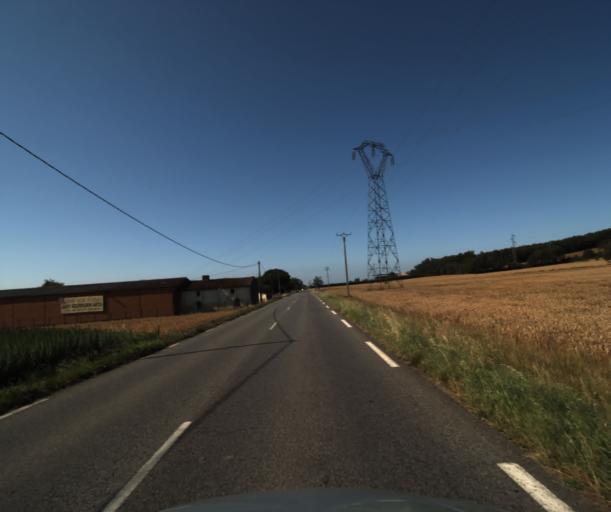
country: FR
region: Midi-Pyrenees
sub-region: Departement de la Haute-Garonne
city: Lagardelle-sur-Leze
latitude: 43.4281
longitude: 1.3775
